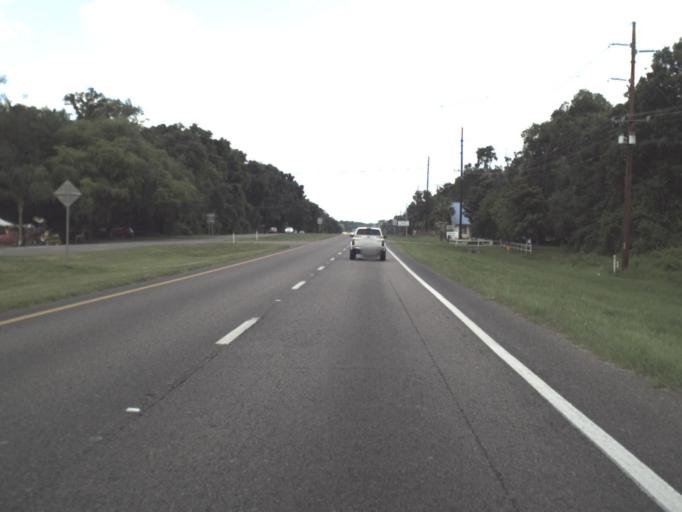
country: US
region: Florida
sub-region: Putnam County
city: East Palatka
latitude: 29.6111
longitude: -81.5836
